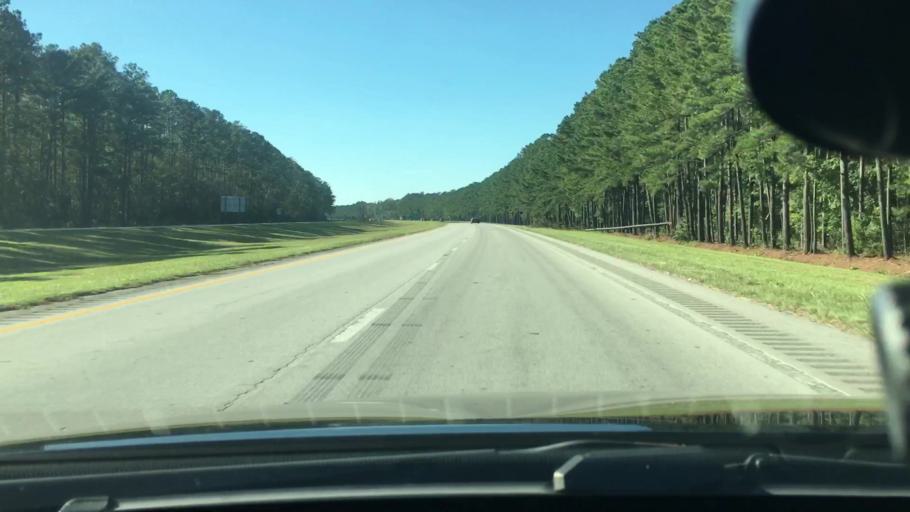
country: US
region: North Carolina
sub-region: Craven County
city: Trent Woods
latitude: 35.1172
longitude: -77.1042
